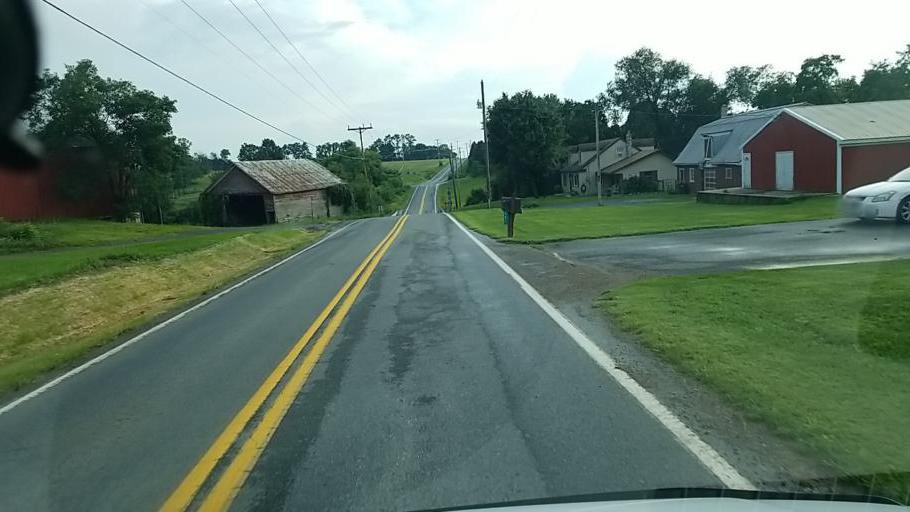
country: US
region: Pennsylvania
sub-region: Cumberland County
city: Newville
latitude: 40.2233
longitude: -77.4590
